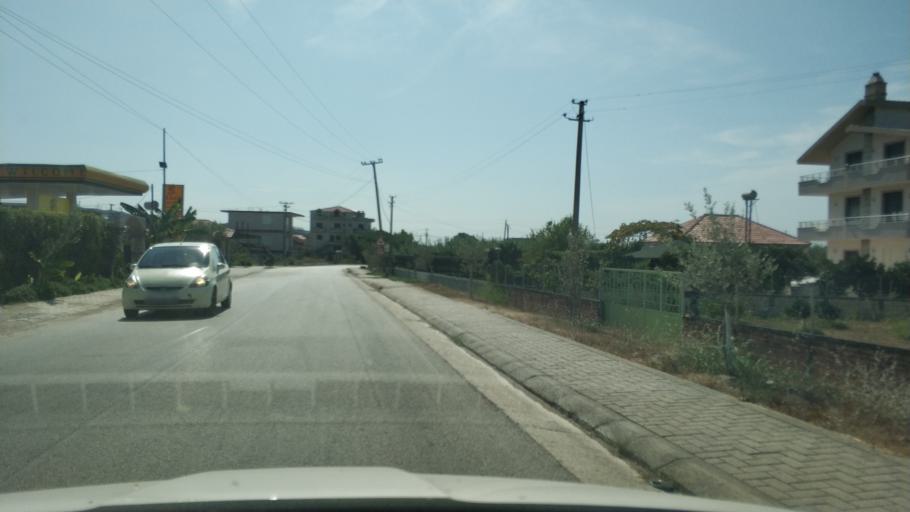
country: AL
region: Fier
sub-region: Rrethi i Lushnjes
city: Divjake
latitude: 40.9787
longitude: 19.5354
